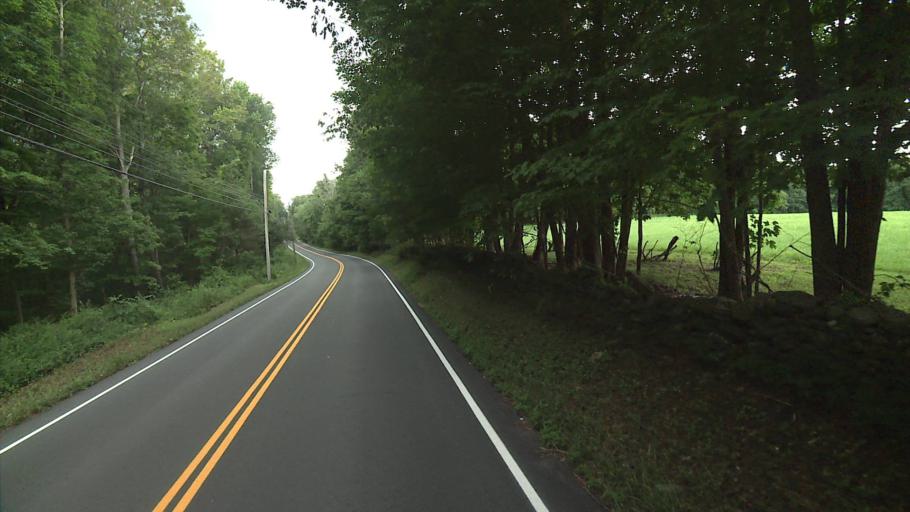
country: US
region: Connecticut
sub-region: New Haven County
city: Heritage Village
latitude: 41.5501
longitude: -73.2966
